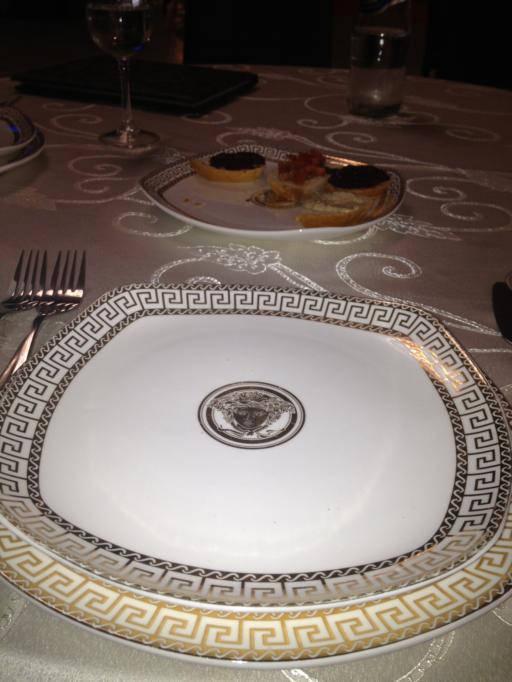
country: AL
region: Tirane
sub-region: Rrethi i Kavajes
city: Golem
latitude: 41.2807
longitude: 19.5135
